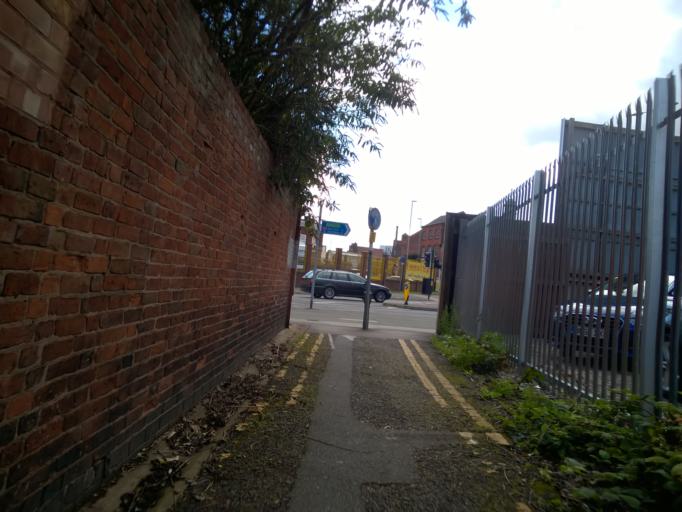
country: GB
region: England
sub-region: City of Leicester
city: Leicester
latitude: 52.6396
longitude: -1.1411
